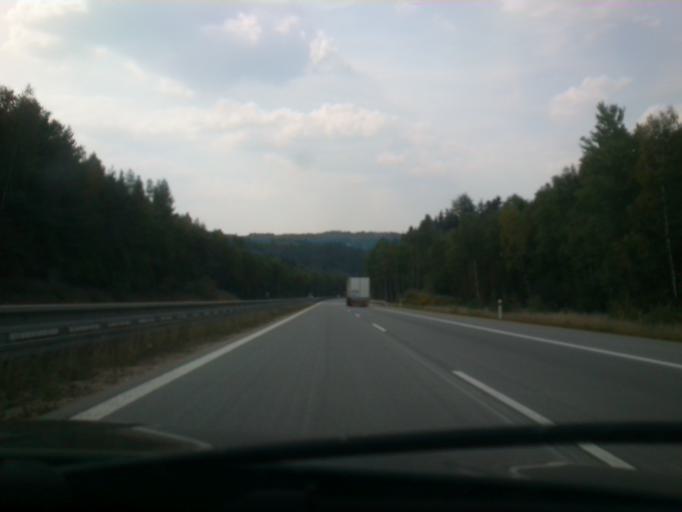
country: CZ
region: Central Bohemia
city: Divisov
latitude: 49.7716
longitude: 14.9421
